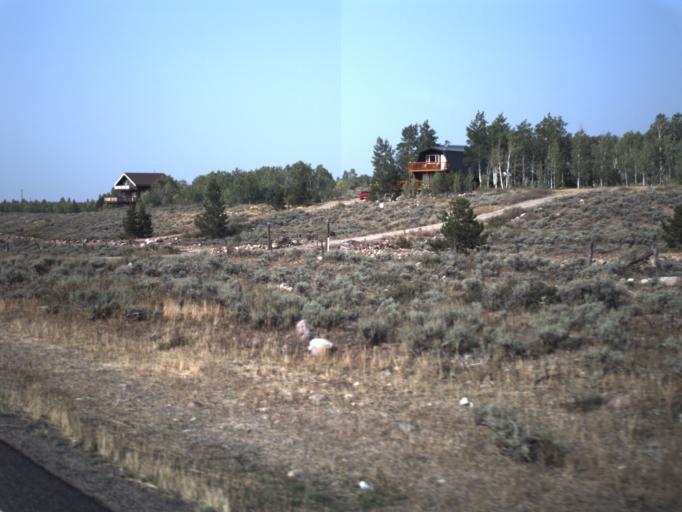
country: US
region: Wyoming
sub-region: Uinta County
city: Evanston
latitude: 40.9349
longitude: -110.8346
